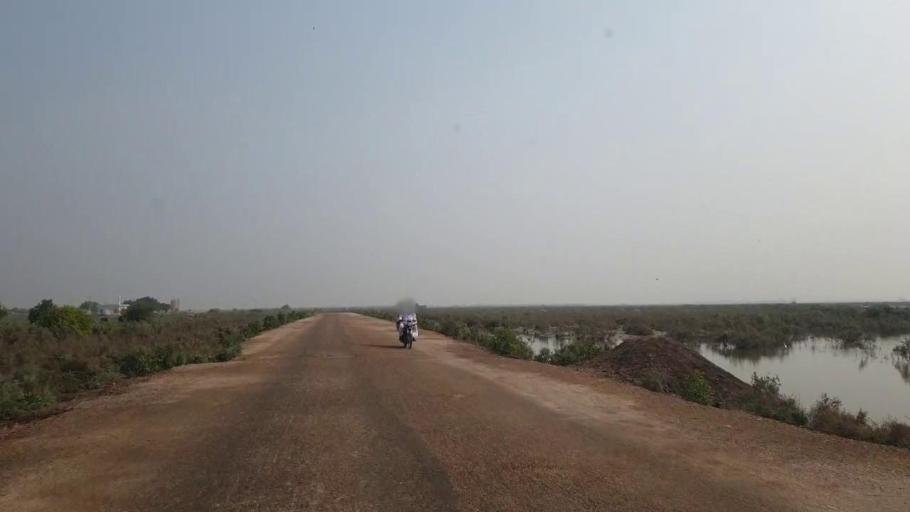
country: PK
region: Sindh
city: Matli
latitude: 25.0975
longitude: 68.6698
